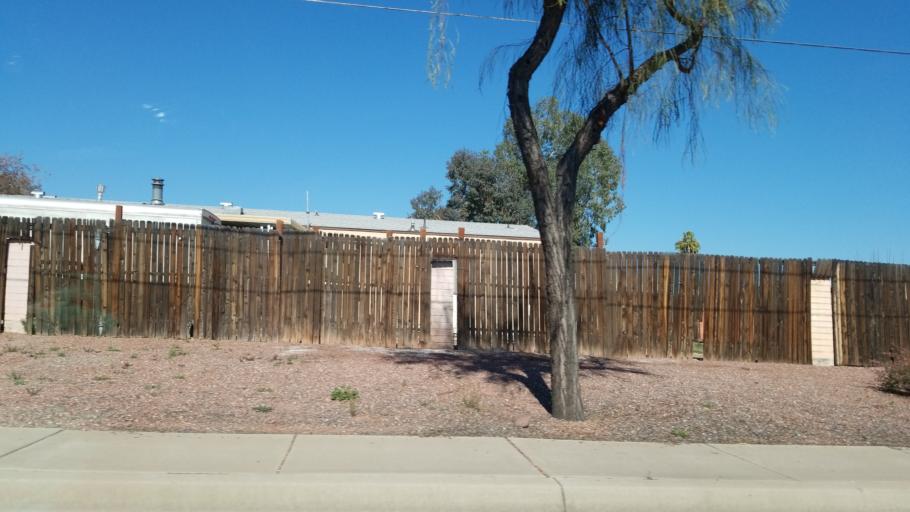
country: US
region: Arizona
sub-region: Maricopa County
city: Glendale
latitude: 33.6475
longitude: -112.0705
